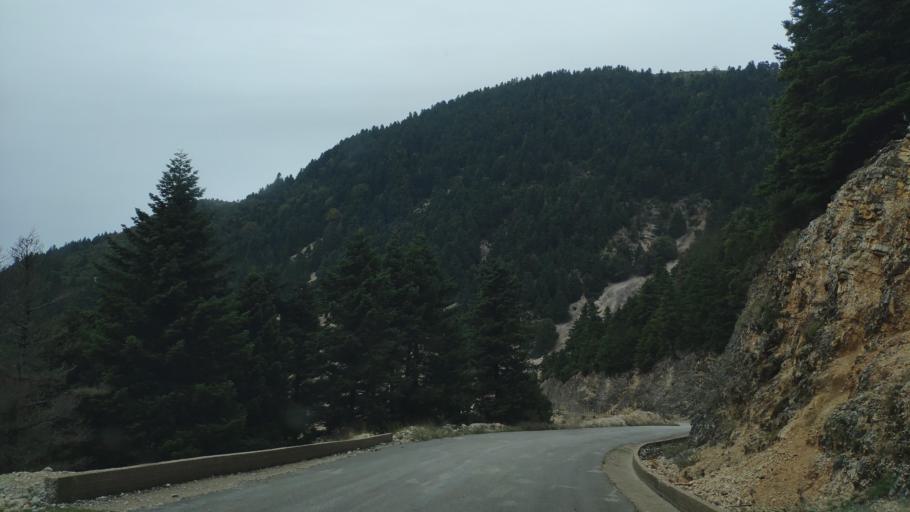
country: GR
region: Epirus
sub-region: Nomos Thesprotias
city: Paramythia
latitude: 39.4433
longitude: 20.6359
